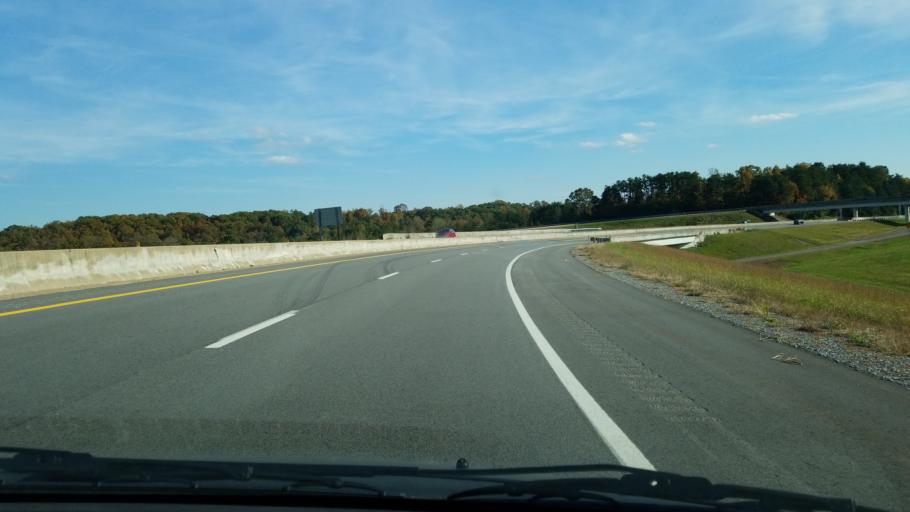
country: US
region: Tennessee
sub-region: Hamilton County
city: Soddy-Daisy
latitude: 35.3027
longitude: -85.1519
